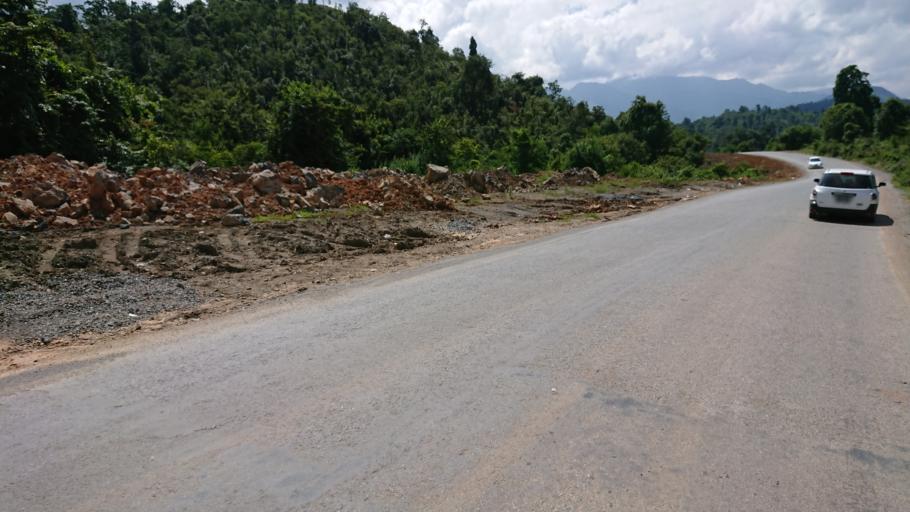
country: MM
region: Shan
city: Taunggyi
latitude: 20.8160
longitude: 97.3171
